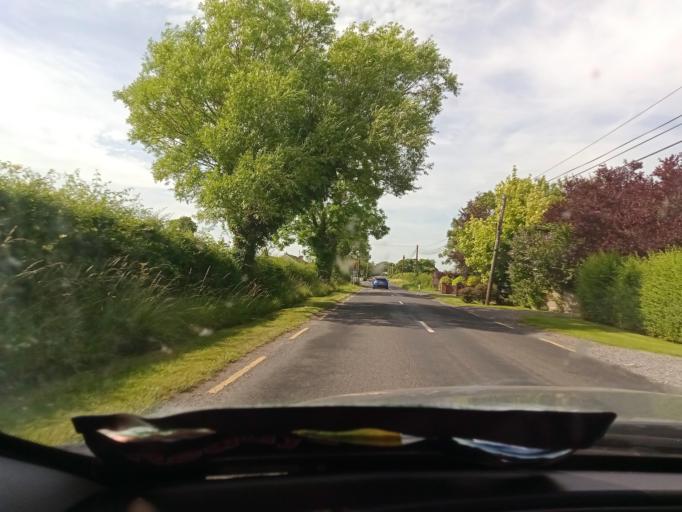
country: IE
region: Leinster
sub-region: Laois
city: Mountmellick
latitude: 53.1055
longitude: -7.3408
